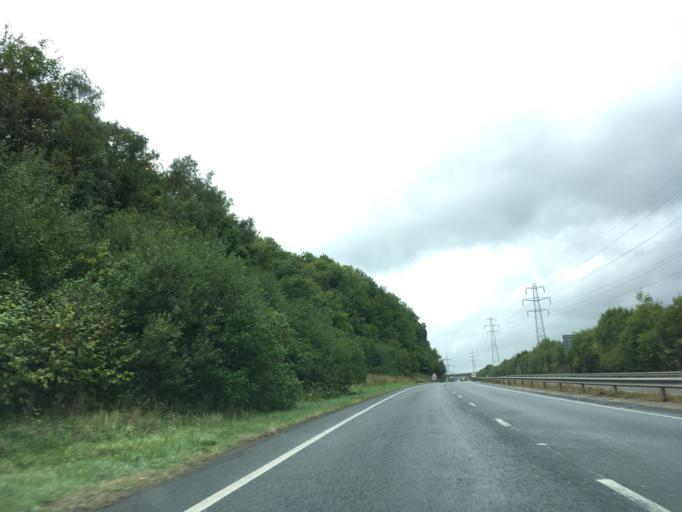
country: GB
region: Wales
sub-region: Monmouthshire
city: Abergavenny
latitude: 51.8179
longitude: -3.0405
